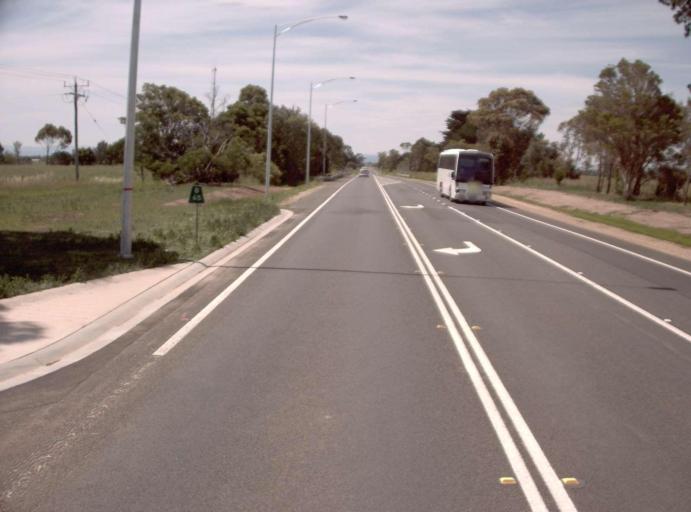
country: AU
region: Victoria
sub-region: Wellington
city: Sale
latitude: -38.0796
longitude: 147.0716
